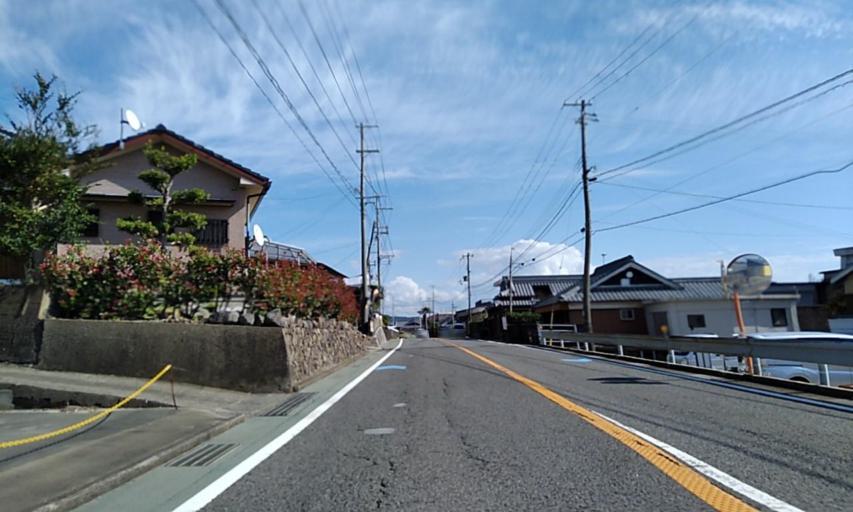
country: JP
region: Wakayama
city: Gobo
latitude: 33.8156
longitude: 135.2005
